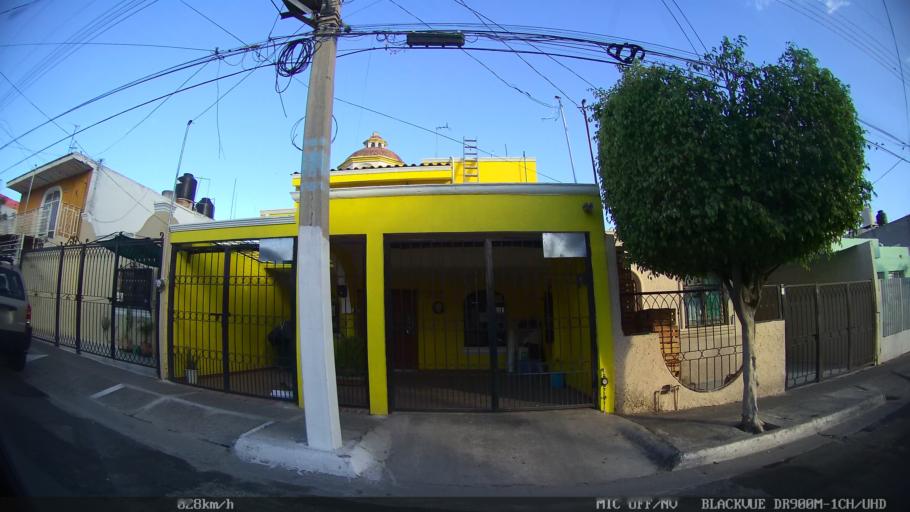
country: MX
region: Jalisco
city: Tlaquepaque
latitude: 20.7109
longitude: -103.3040
